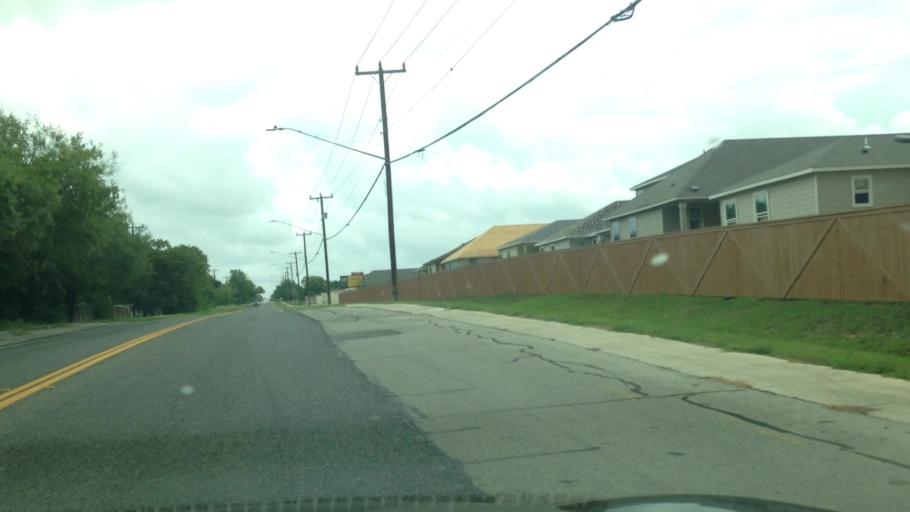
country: US
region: Texas
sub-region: Bexar County
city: Live Oak
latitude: 29.5764
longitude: -98.3985
